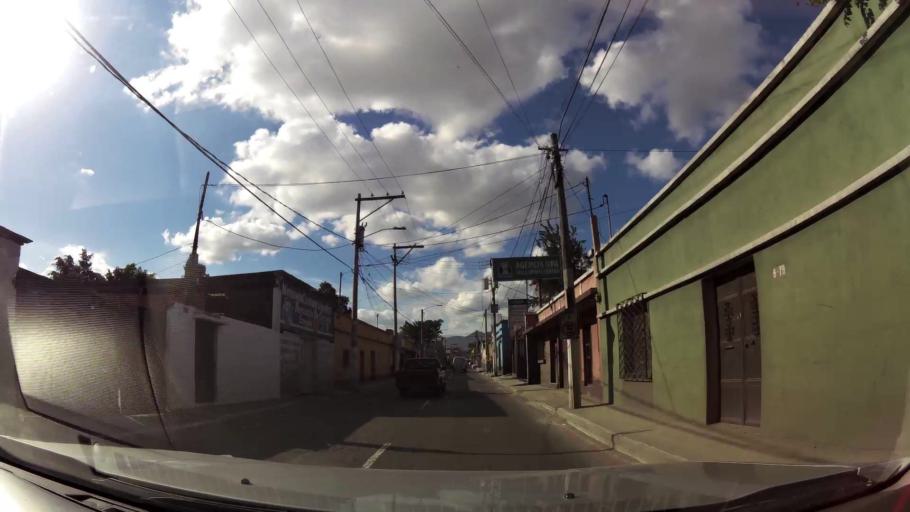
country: GT
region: Guatemala
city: Villa Nueva
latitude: 14.5233
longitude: -90.5859
